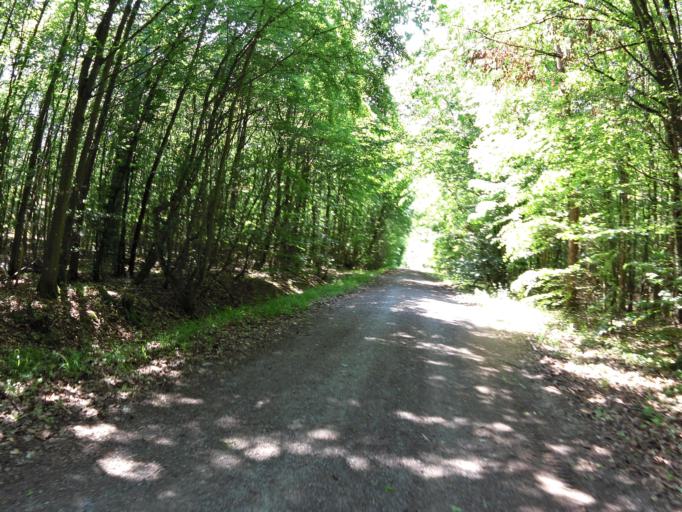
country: DE
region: Bavaria
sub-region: Regierungsbezirk Unterfranken
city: Kist
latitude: 49.7257
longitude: 9.8536
